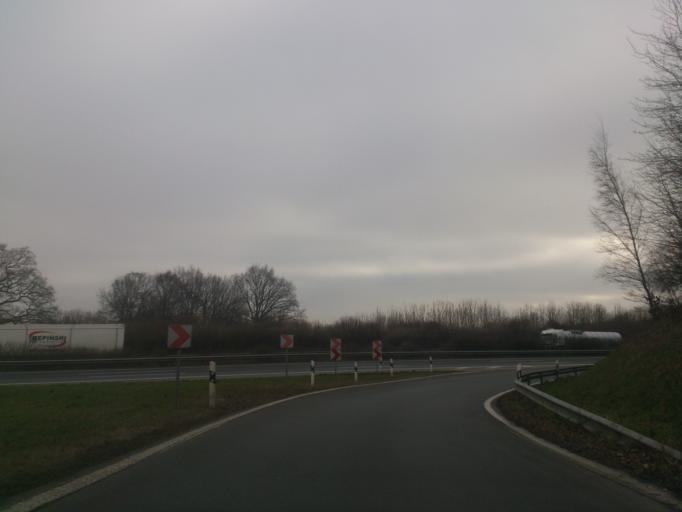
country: DE
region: North Rhine-Westphalia
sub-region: Regierungsbezirk Detmold
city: Bad Salzuflen
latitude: 52.1431
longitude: 8.7805
